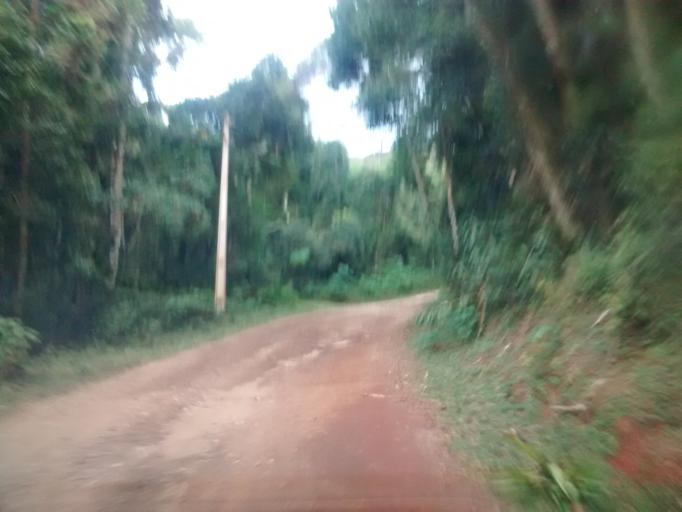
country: BR
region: Sao Paulo
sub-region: Campos Do Jordao
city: Campos do Jordao
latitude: -22.6818
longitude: -45.6390
